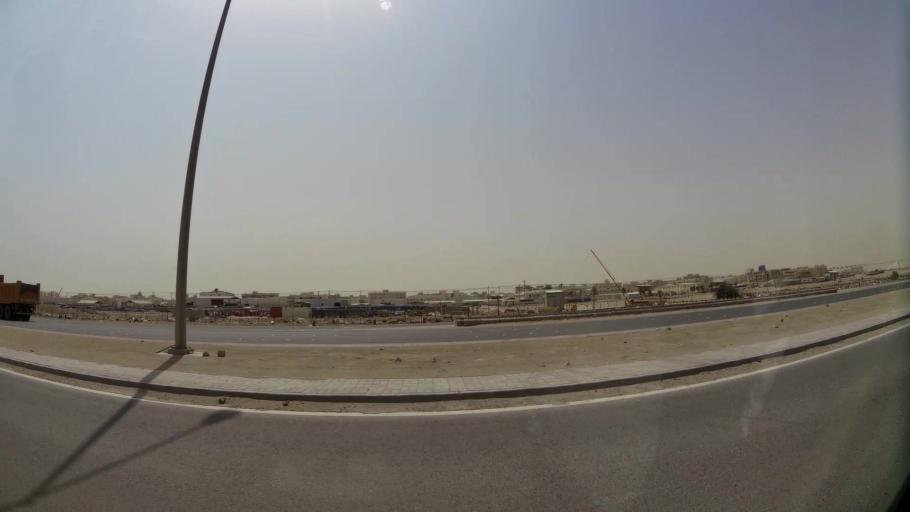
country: QA
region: Baladiyat ar Rayyan
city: Ar Rayyan
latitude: 25.1820
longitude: 51.4195
